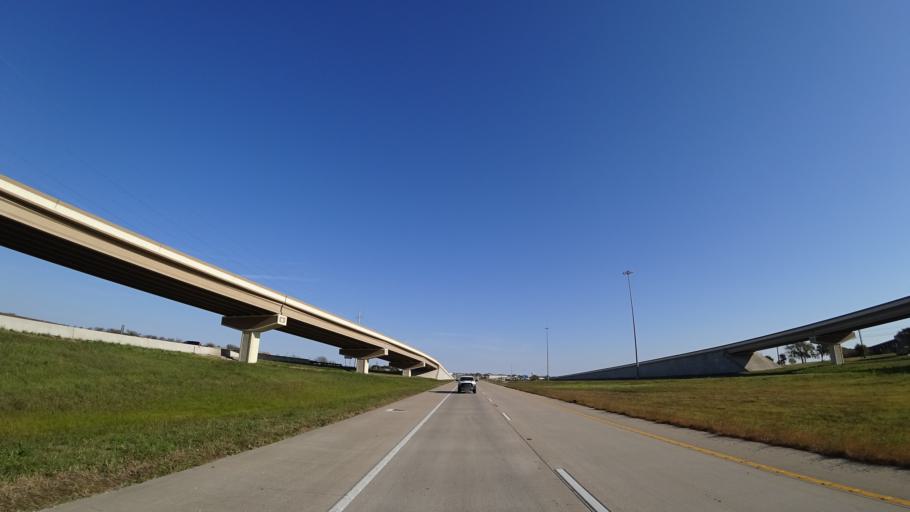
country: US
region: Texas
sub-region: Travis County
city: Pflugerville
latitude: 30.4761
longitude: -97.5904
